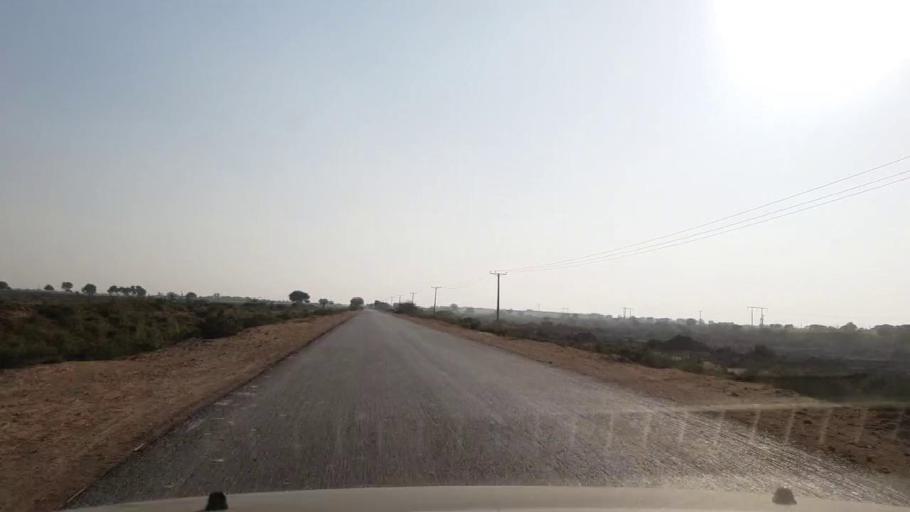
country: PK
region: Sindh
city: Bulri
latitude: 24.9113
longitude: 68.3483
